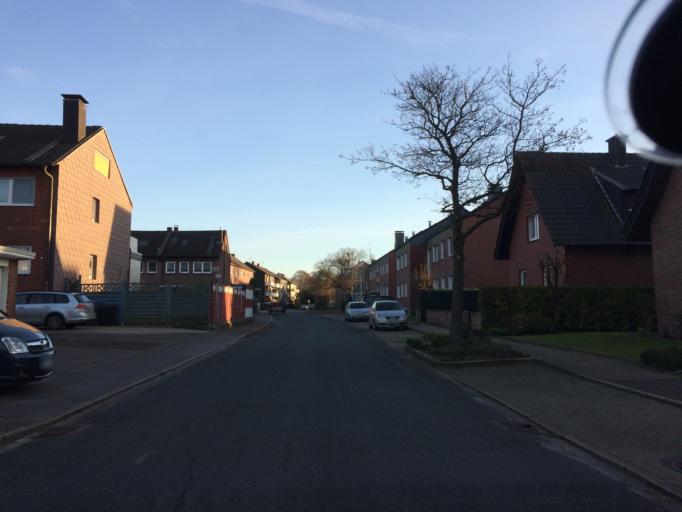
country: DE
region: North Rhine-Westphalia
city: Dorsten
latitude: 51.6767
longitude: 7.0079
